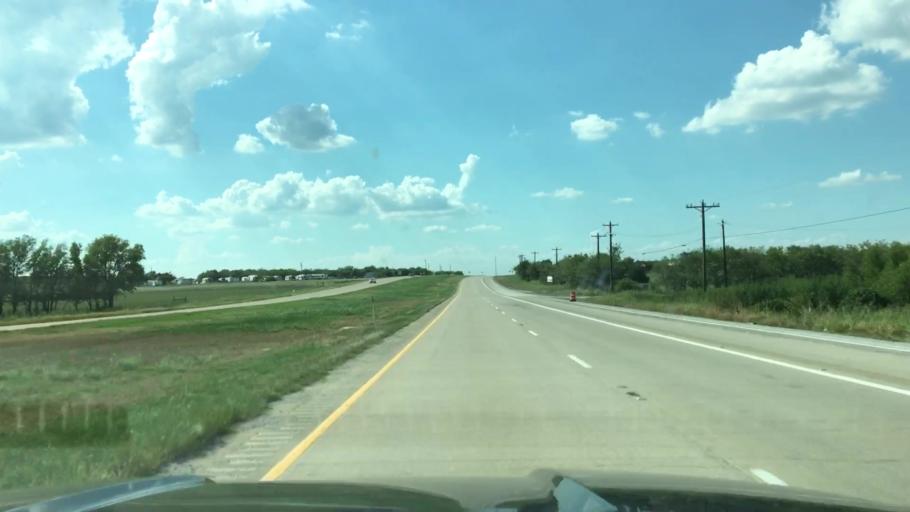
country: US
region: Texas
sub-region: Wise County
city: Rhome
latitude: 33.0401
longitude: -97.4457
